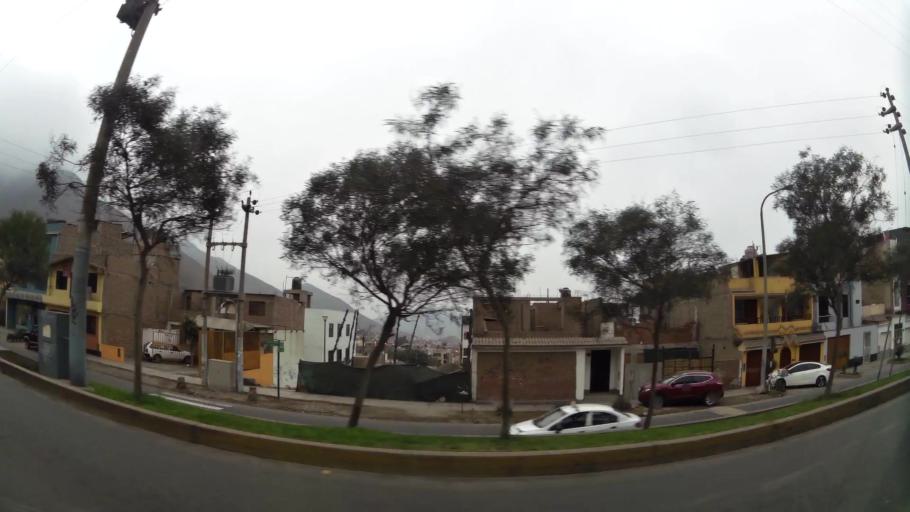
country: PE
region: Lima
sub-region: Lima
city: La Molina
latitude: -12.1155
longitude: -76.9382
